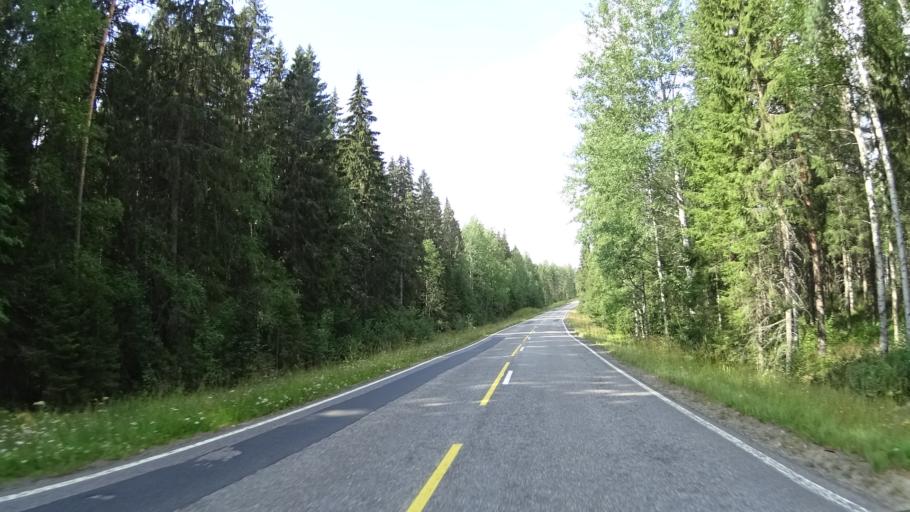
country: FI
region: Pirkanmaa
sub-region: Tampere
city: Luopioinen
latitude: 61.4821
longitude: 24.7513
